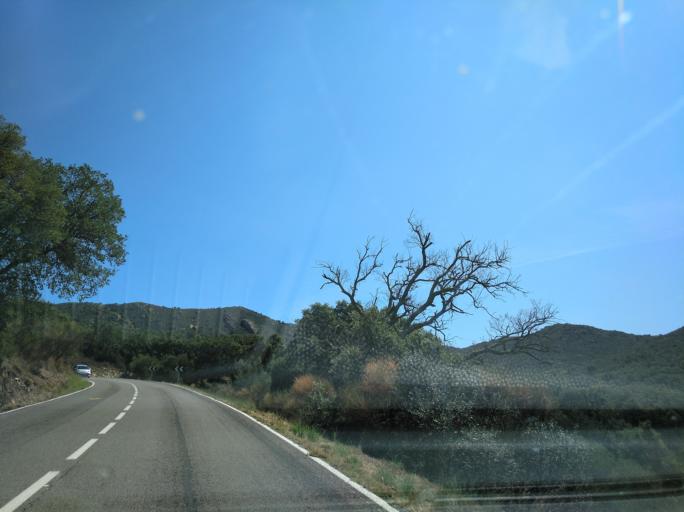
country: ES
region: Catalonia
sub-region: Provincia de Girona
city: Pau
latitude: 42.3307
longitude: 3.1132
